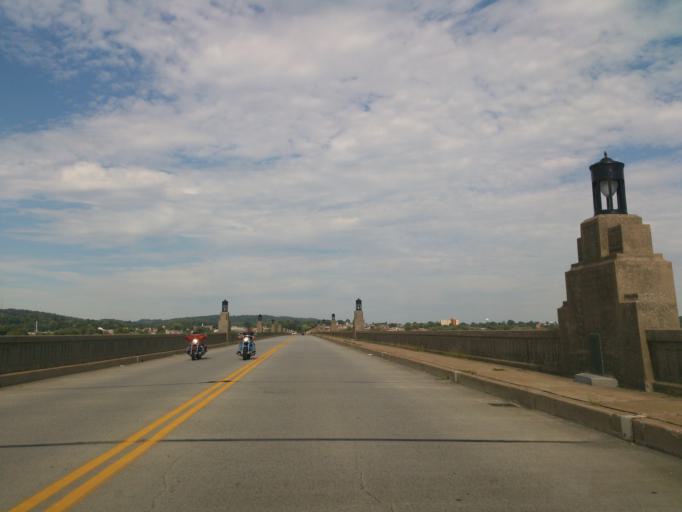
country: US
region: Pennsylvania
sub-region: York County
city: Wrightsville
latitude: 40.0276
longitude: -76.5210
